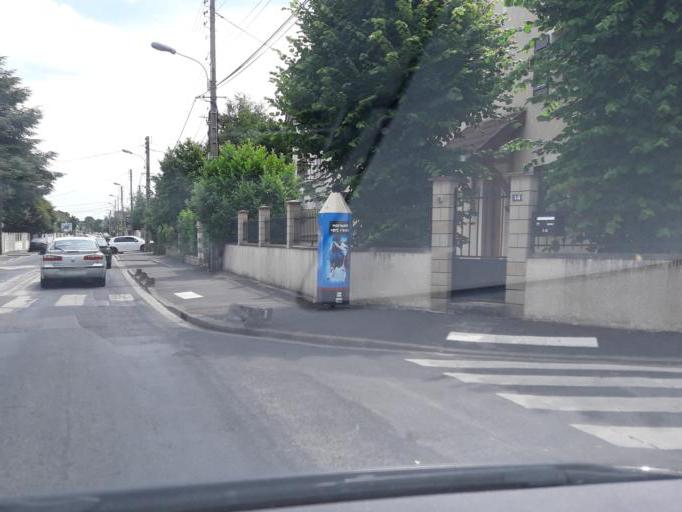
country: FR
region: Ile-de-France
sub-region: Departement de l'Essonne
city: Morsang-sur-Orge
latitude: 48.6456
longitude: 2.3491
